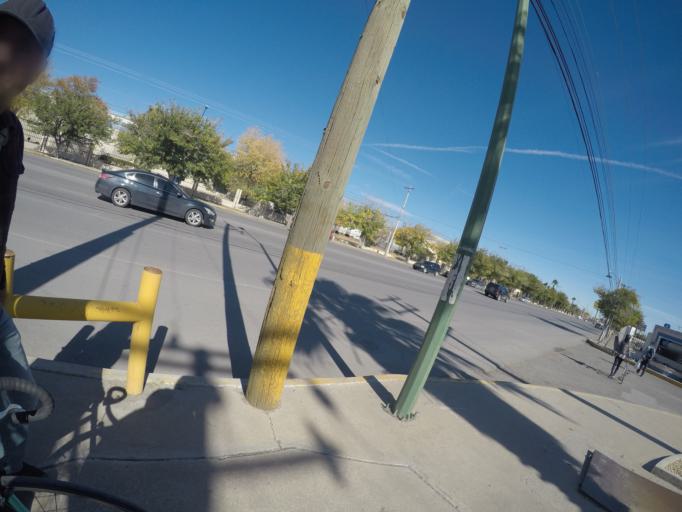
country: MX
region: Chihuahua
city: Ciudad Juarez
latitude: 31.7330
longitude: -106.4177
